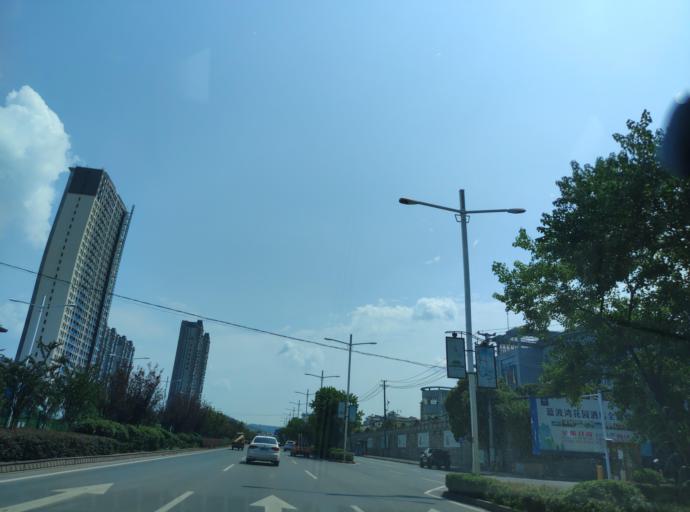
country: CN
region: Jiangxi Sheng
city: Pingxiang
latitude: 27.6544
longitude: 113.8872
